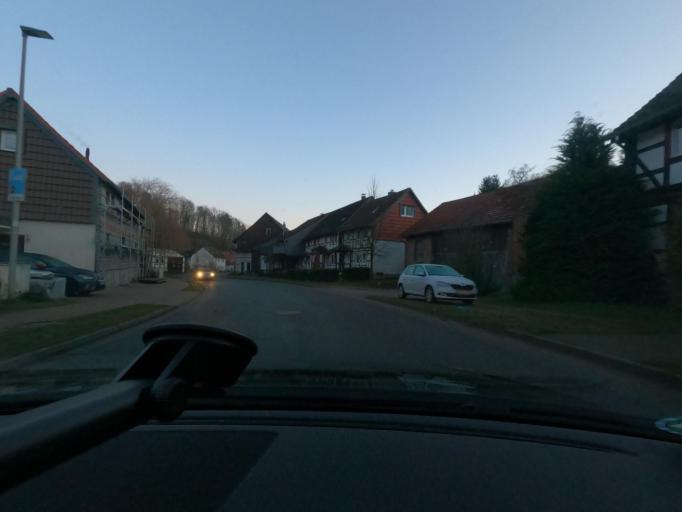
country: DE
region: Lower Saxony
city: Eisdorf am Harz
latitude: 51.7768
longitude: 10.1704
